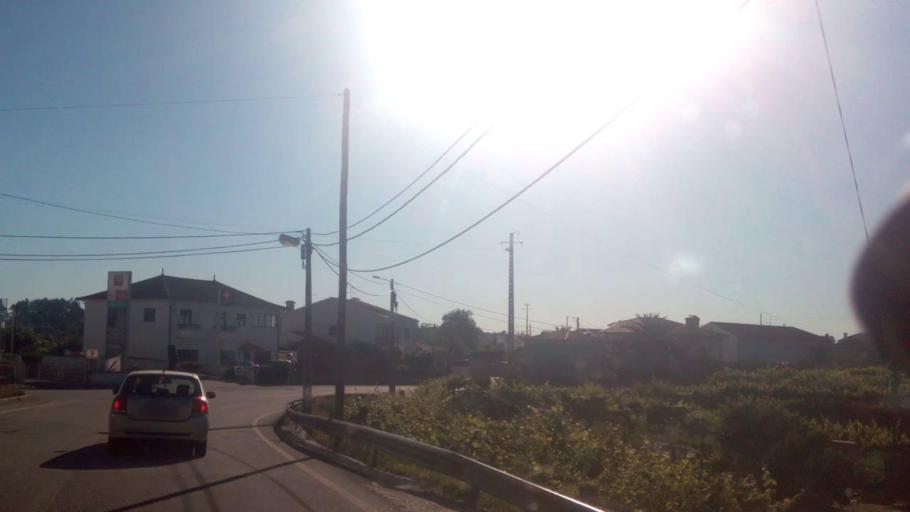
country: PT
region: Porto
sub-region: Penafiel
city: Perafita
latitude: 41.1859
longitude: -8.2649
